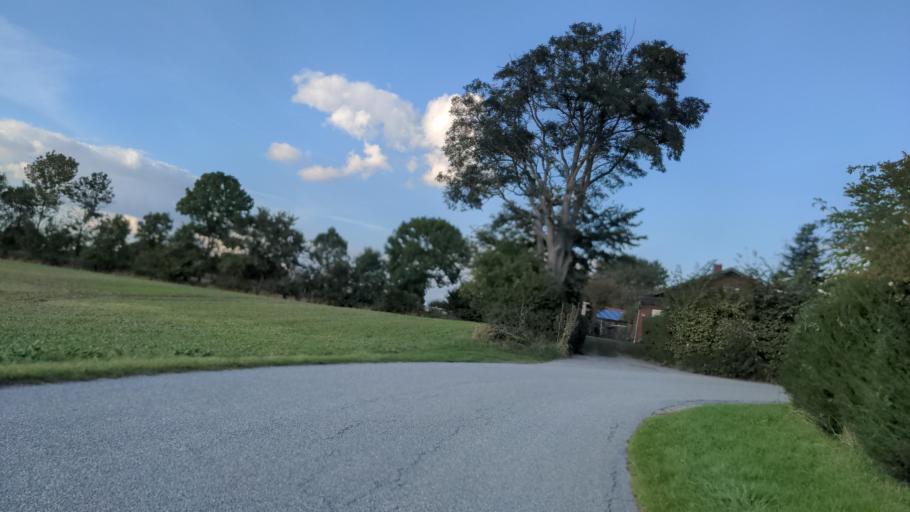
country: DE
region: Schleswig-Holstein
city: Ahrensbok
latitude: 53.9926
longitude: 10.6227
